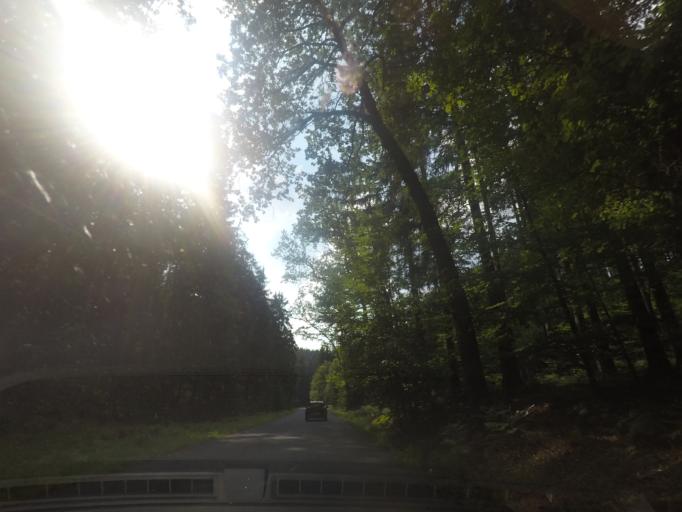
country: DE
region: Saxony
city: Sebnitz
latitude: 50.8754
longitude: 14.2941
